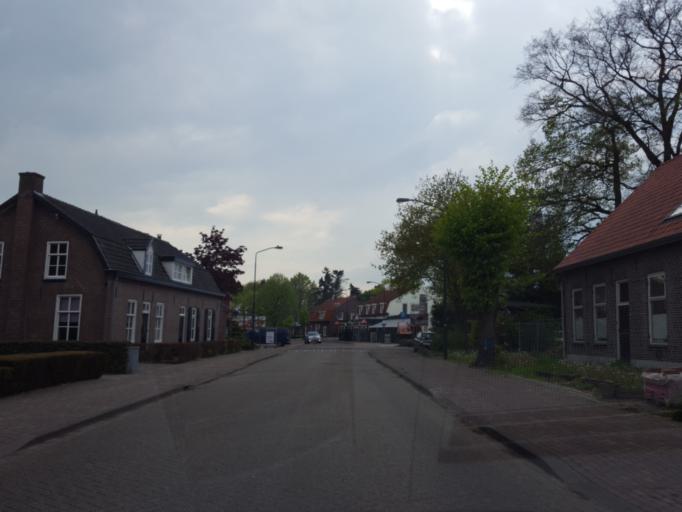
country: NL
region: North Brabant
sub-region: Gemeente Cranendonck
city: Cranendonck
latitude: 51.3041
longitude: 5.5740
